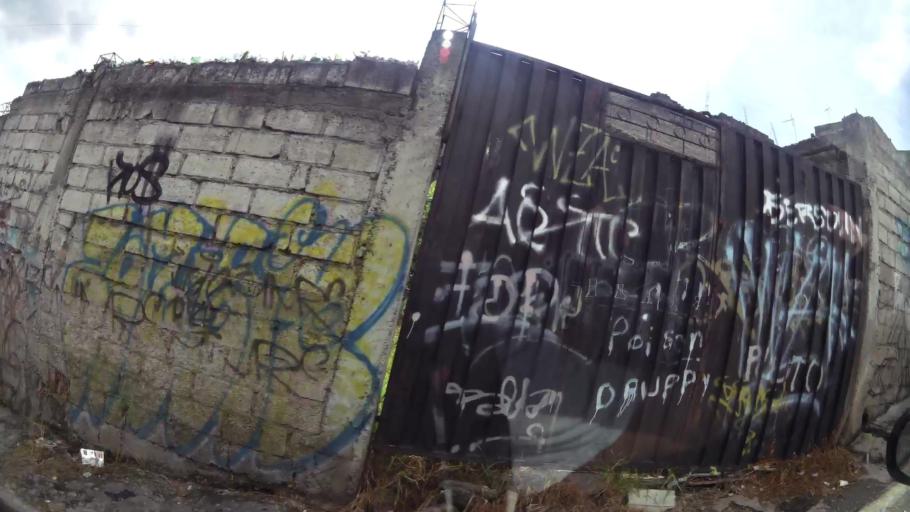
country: EC
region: Pichincha
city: Quito
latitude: -0.2581
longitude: -78.5204
